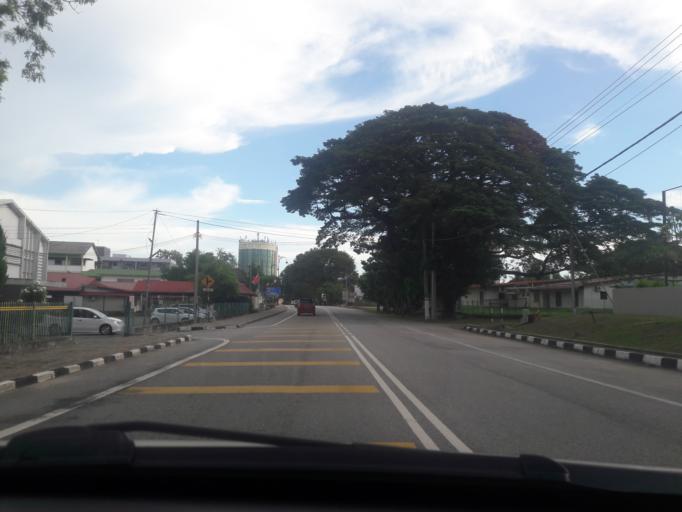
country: MY
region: Kedah
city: Sungai Petani
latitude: 5.6495
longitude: 100.4890
